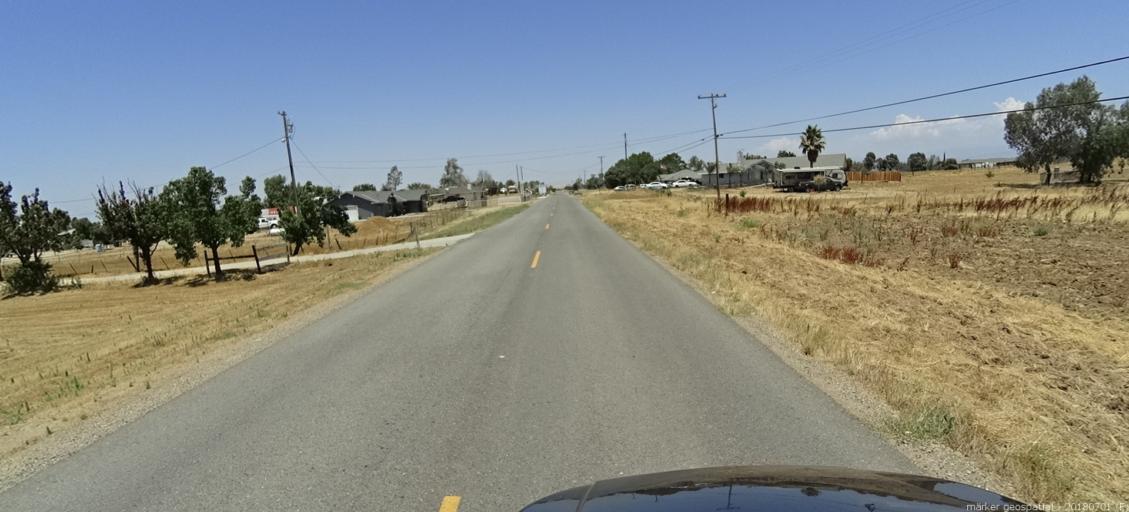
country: US
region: California
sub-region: Madera County
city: Madera Acres
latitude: 37.0423
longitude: -119.9927
